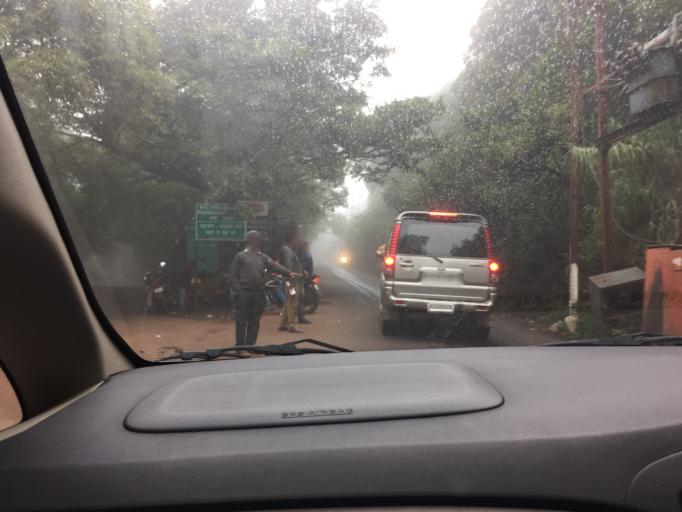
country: IN
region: Maharashtra
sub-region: Satara Division
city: Mahabaleshwar
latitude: 17.9198
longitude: 73.6701
